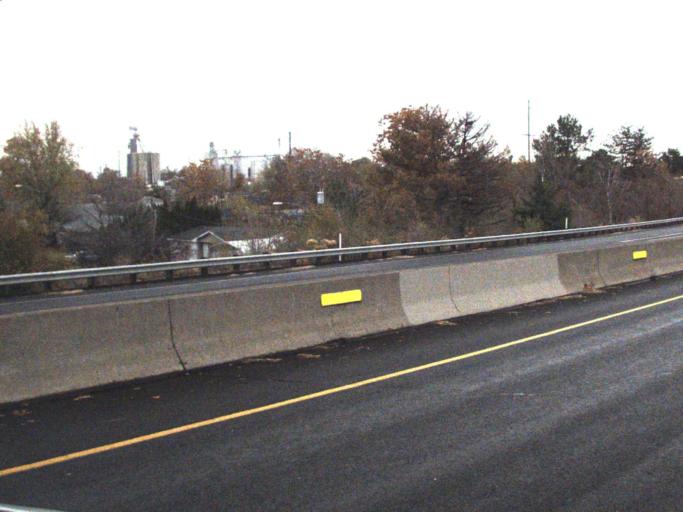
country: US
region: Washington
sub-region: Walla Walla County
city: Walla Walla
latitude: 46.0703
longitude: -118.3495
